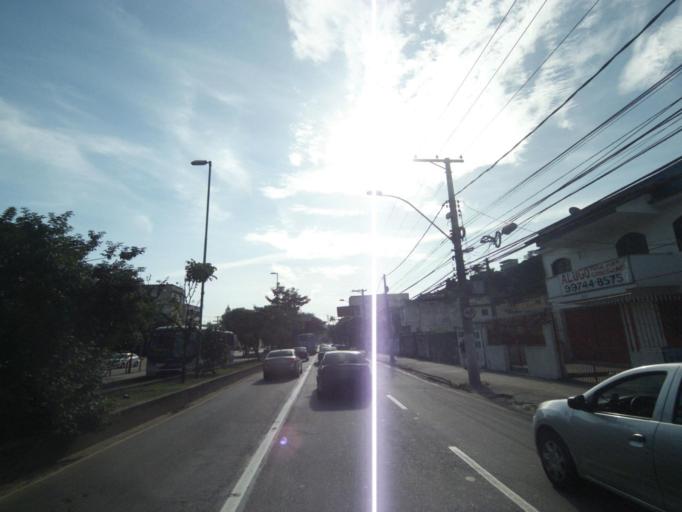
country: BR
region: Rio de Janeiro
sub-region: Niteroi
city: Niteroi
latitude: -22.8806
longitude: -43.1043
